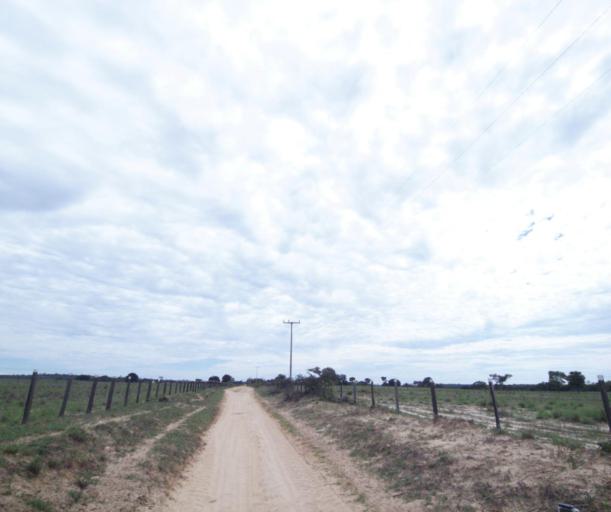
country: BR
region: Bahia
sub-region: Carinhanha
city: Carinhanha
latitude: -14.2545
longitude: -44.3571
